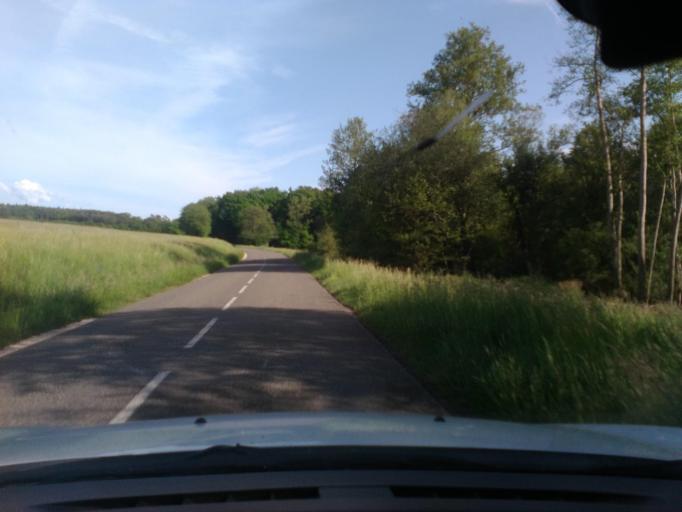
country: FR
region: Lorraine
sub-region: Departement des Vosges
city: Jeanmenil
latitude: 48.2907
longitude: 6.6926
